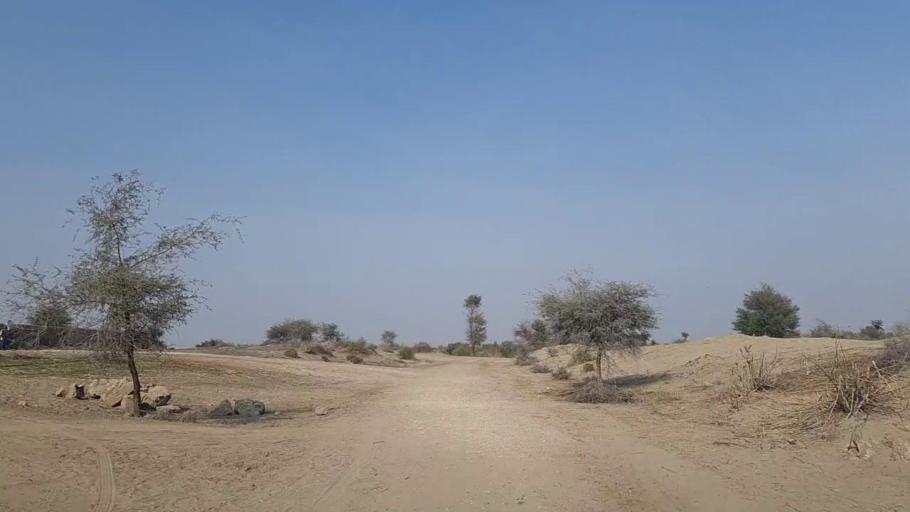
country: PK
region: Sindh
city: Daur
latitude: 26.5167
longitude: 68.4812
